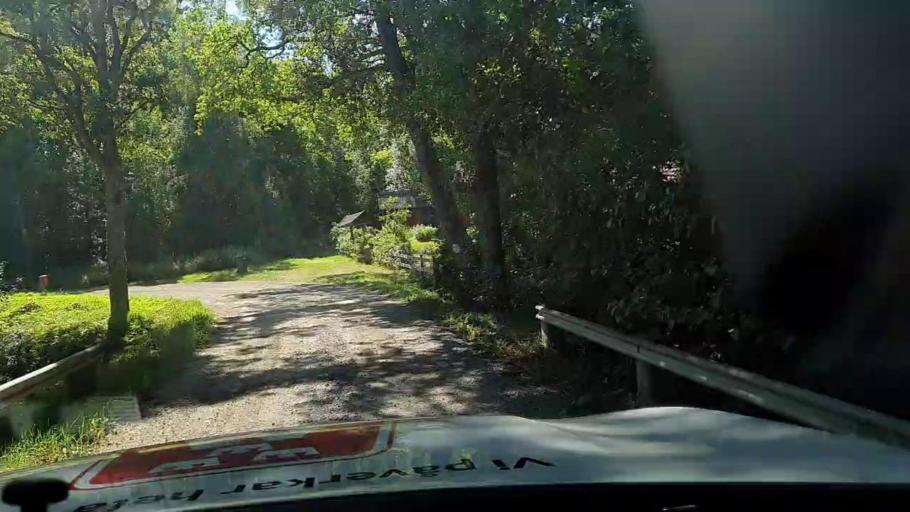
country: SE
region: Soedermanland
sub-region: Strangnas Kommun
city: Akers Styckebruk
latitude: 59.2118
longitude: 16.9108
